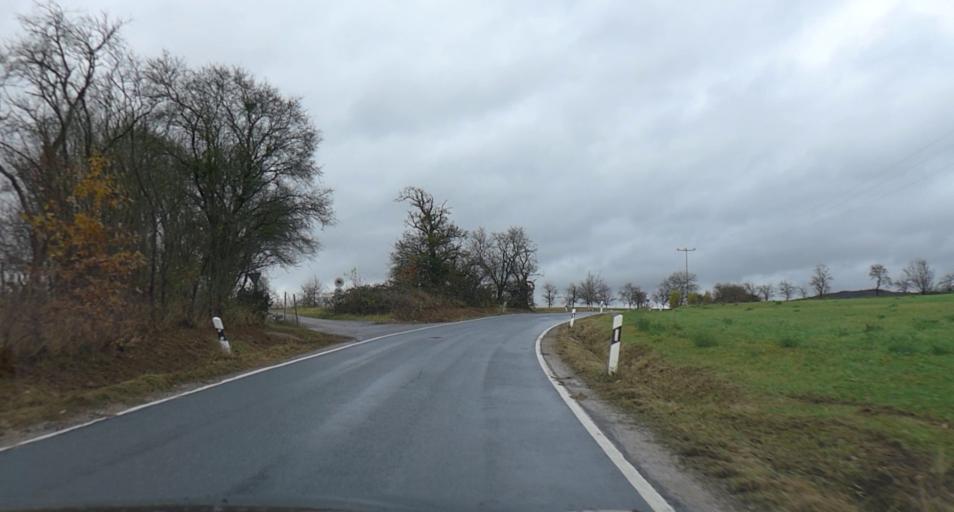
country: DE
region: Bavaria
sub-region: Upper Franconia
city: Kunreuth
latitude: 49.6848
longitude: 11.1488
